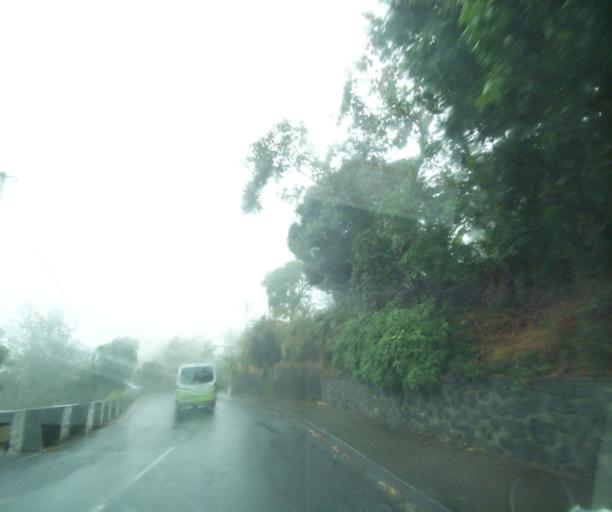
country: RE
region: Reunion
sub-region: Reunion
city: Saint-Paul
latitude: -20.9989
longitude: 55.3261
